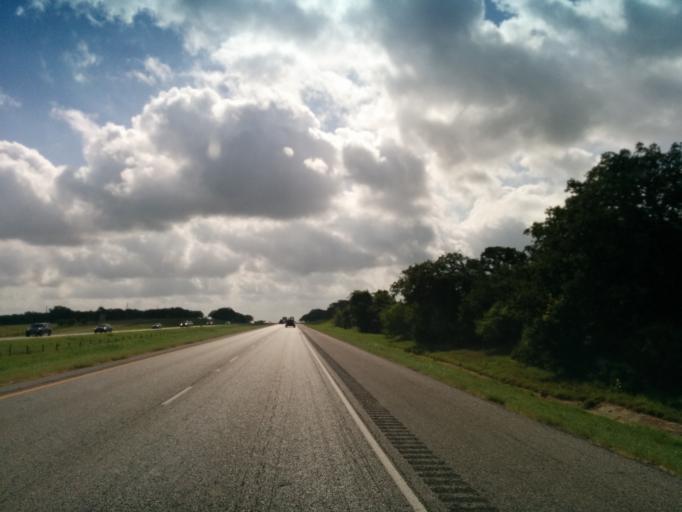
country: US
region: Texas
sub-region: Gonzales County
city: Waelder
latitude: 29.6566
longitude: -97.4304
